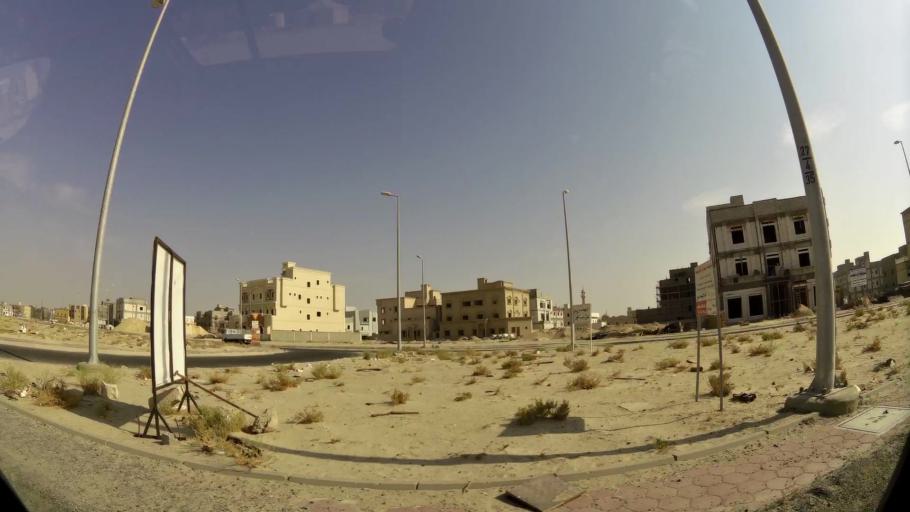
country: KW
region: Al Ahmadi
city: Al Wafrah
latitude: 28.7838
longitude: 48.0506
